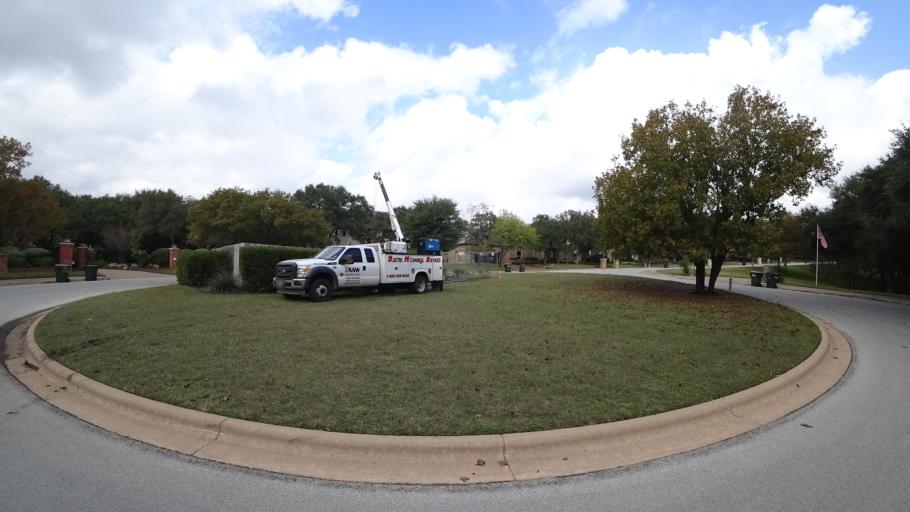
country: US
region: Texas
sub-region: Travis County
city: Barton Creek
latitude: 30.2913
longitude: -97.8991
